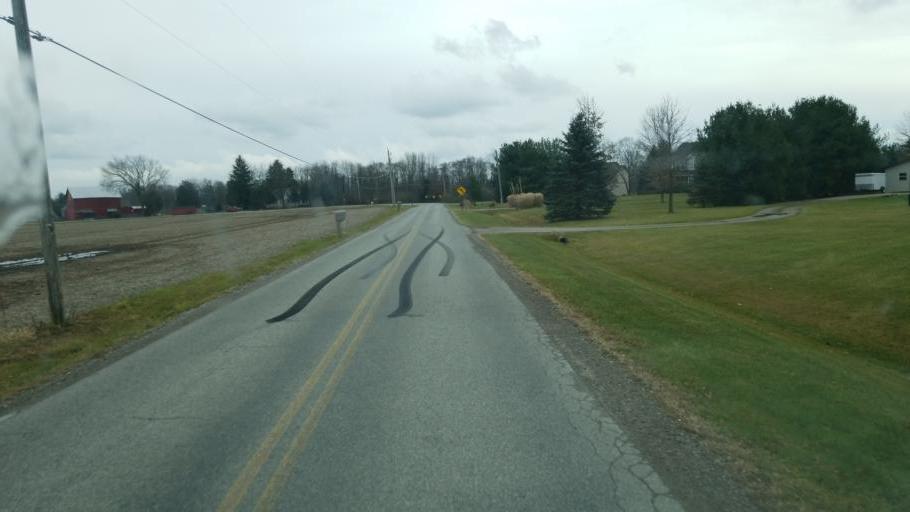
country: US
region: Ohio
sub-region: Delaware County
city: Delaware
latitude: 40.2702
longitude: -83.0028
